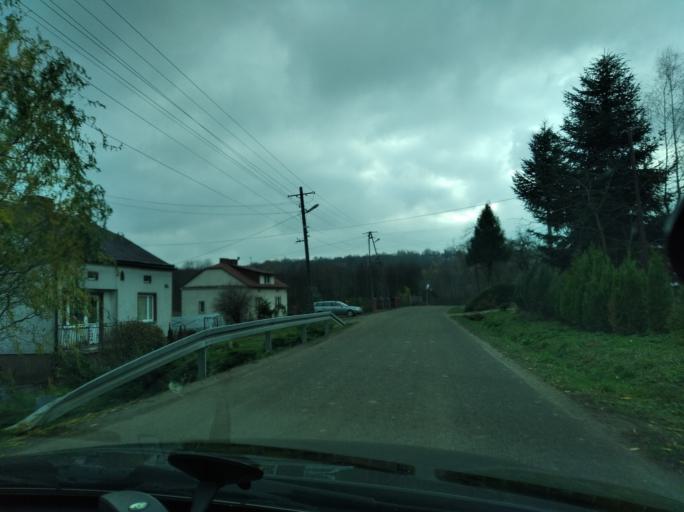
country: PL
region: Subcarpathian Voivodeship
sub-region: Powiat przeworski
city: Sietesz
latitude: 49.9818
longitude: 22.3444
